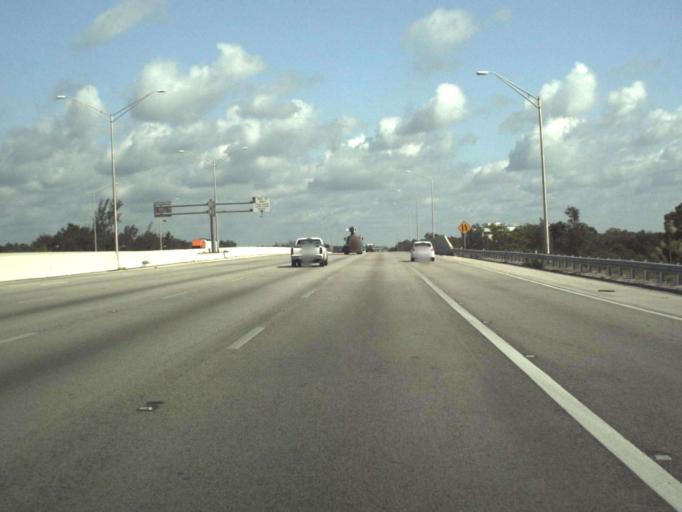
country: US
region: Florida
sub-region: Palm Beach County
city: North Palm Beach
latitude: 26.8427
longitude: -80.1036
